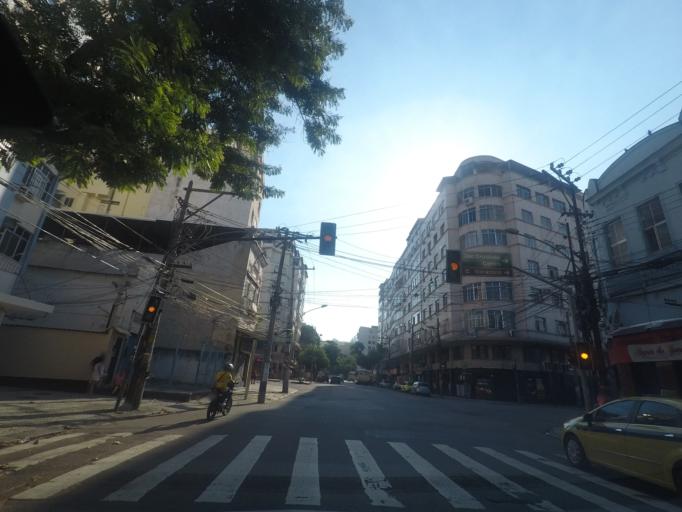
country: BR
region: Rio de Janeiro
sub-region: Rio De Janeiro
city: Rio de Janeiro
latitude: -22.9140
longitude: -43.2185
